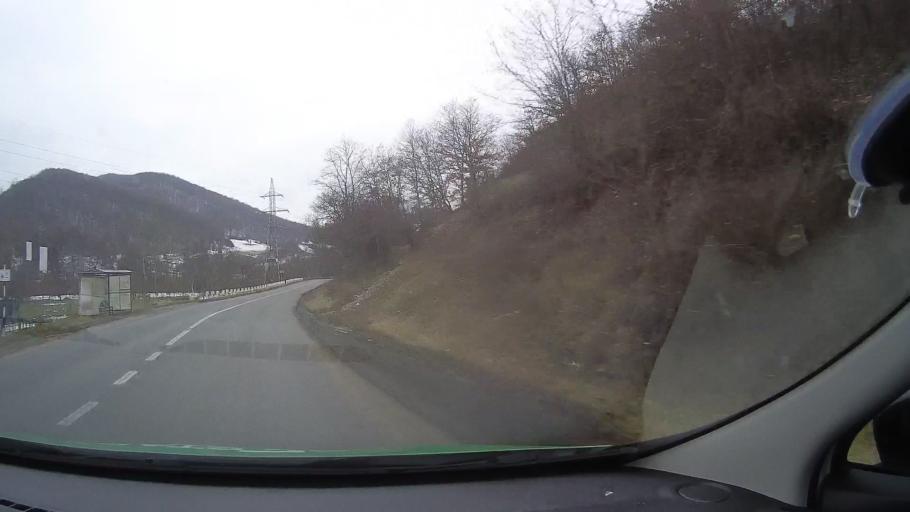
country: RO
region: Alba
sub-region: Comuna Metes
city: Metes
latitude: 46.1010
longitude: 23.4554
